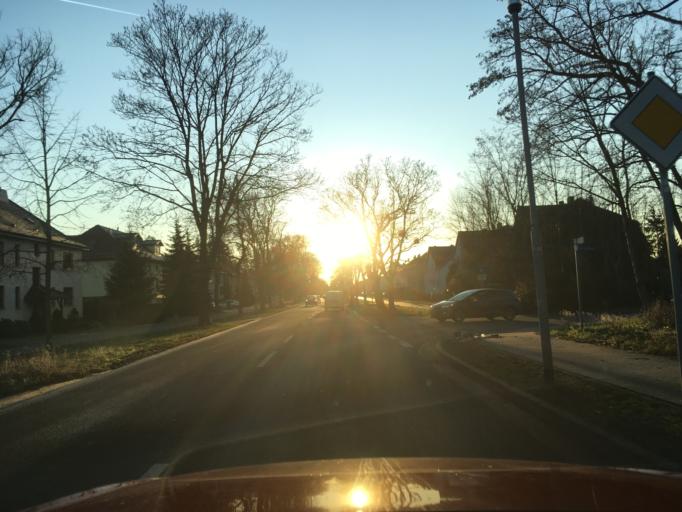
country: DE
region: Saxony-Anhalt
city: Rosslau
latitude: 51.8935
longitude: 12.2647
